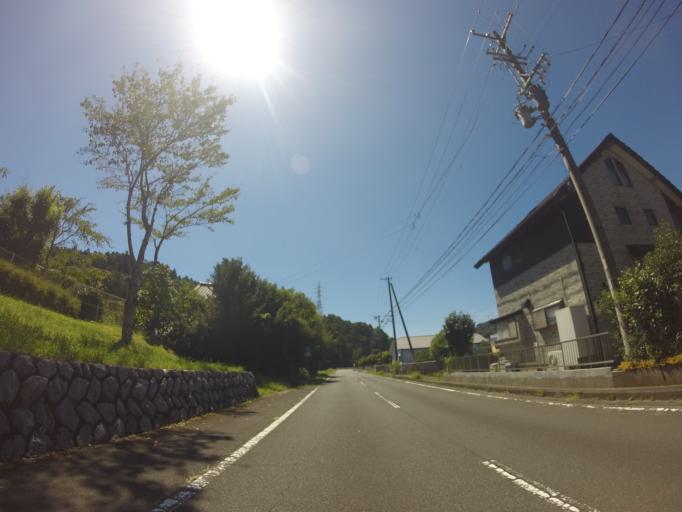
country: JP
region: Shizuoka
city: Kanaya
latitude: 34.8770
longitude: 138.1398
